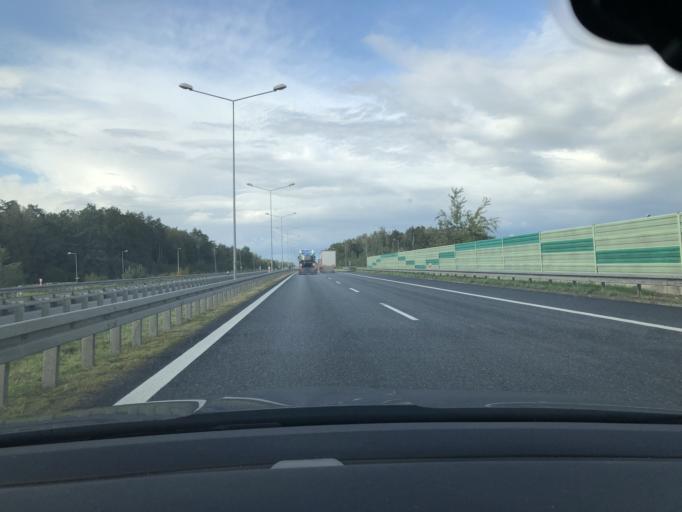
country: PL
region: Silesian Voivodeship
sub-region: Powiat gliwicki
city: Sosnicowice
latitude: 50.3118
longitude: 18.5505
